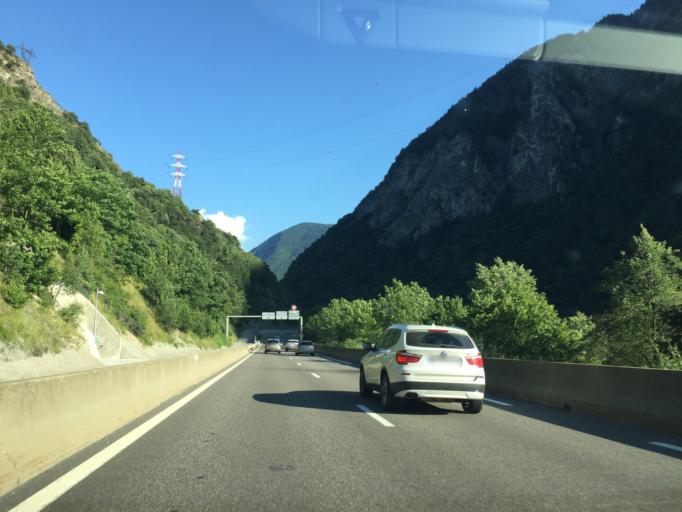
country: FR
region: Rhone-Alpes
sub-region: Departement de la Savoie
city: Aigueblanche
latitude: 45.4922
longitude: 6.5179
